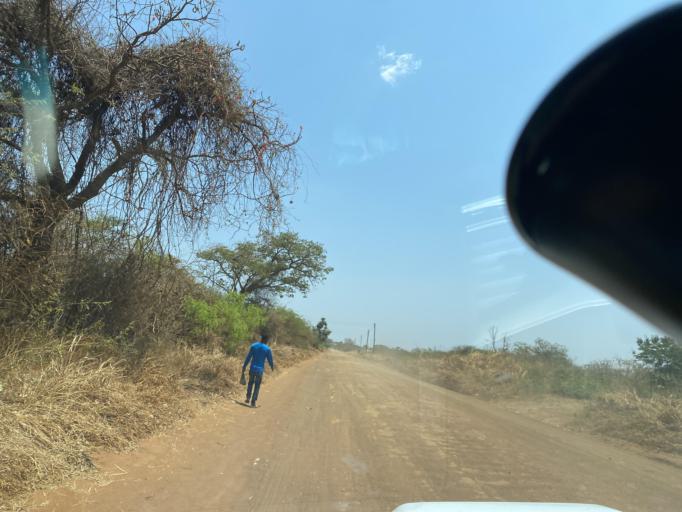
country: ZM
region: Lusaka
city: Lusaka
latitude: -15.4211
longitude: 28.0995
